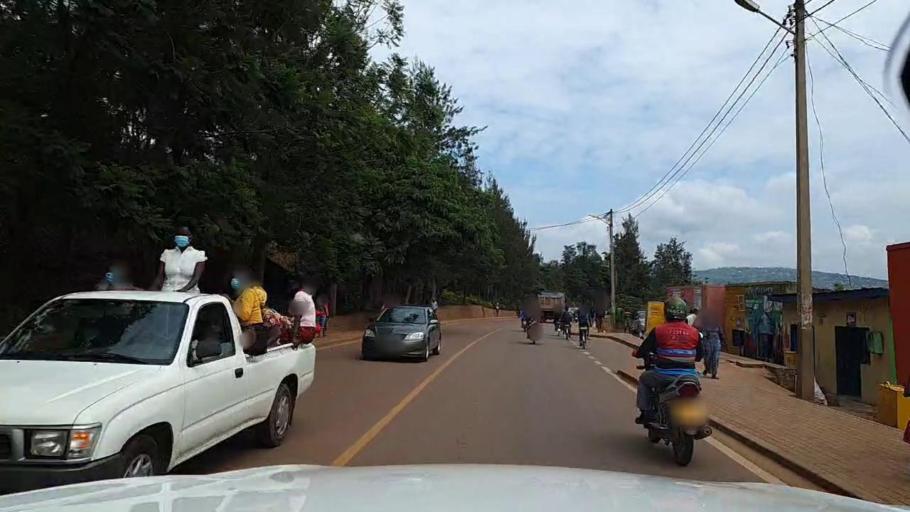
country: RW
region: Kigali
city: Kigali
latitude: -1.9259
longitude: 30.0463
